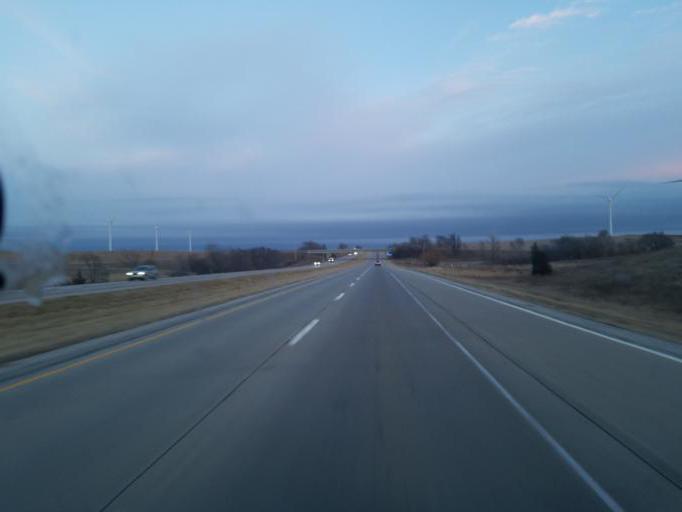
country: US
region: Iowa
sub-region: Pottawattamie County
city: Avoca
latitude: 41.4973
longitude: -95.2554
